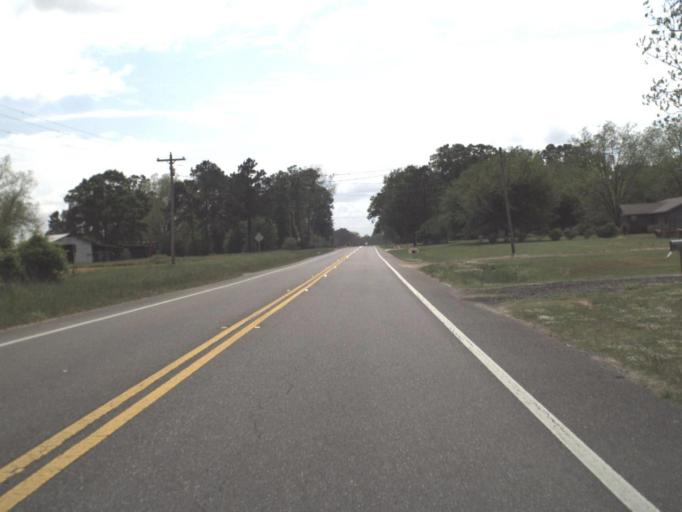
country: US
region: Alabama
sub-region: Escambia County
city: East Brewton
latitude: 30.9803
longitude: -87.1195
